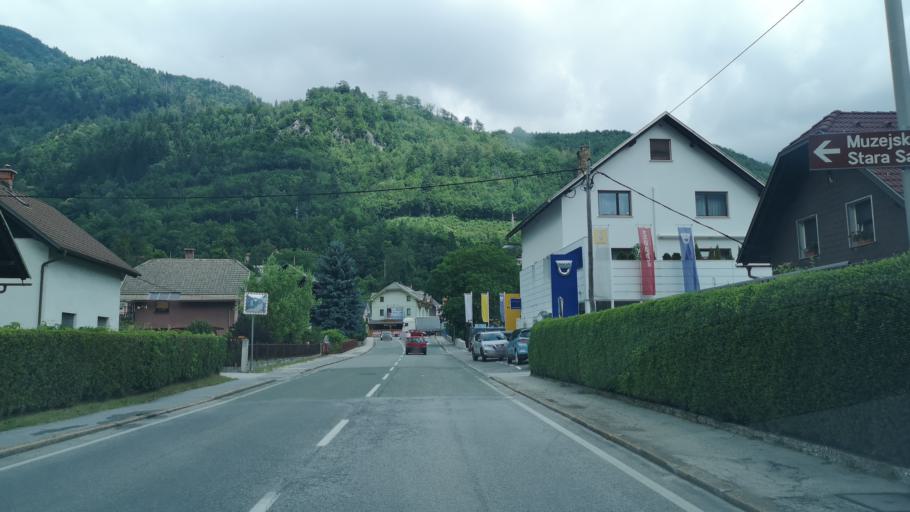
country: SI
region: Jesenice
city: Slovenski Javornik
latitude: 46.4266
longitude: 14.0817
